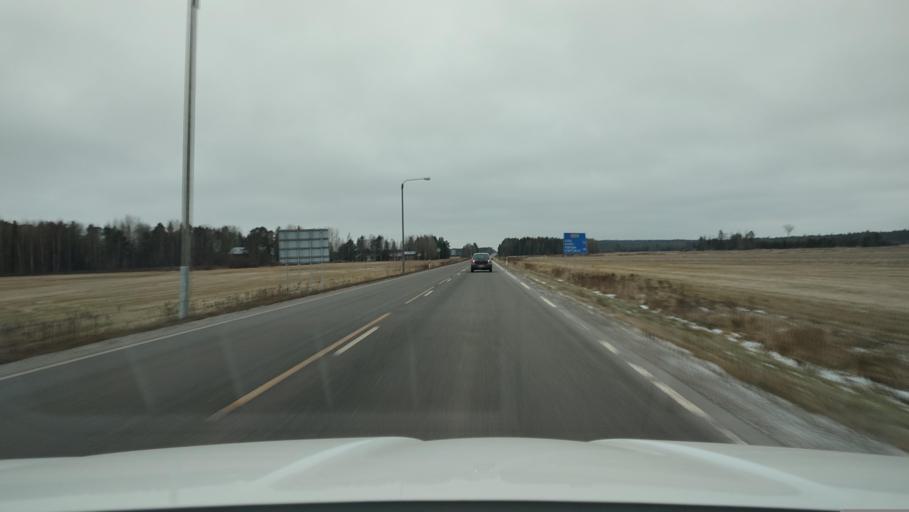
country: FI
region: Ostrobothnia
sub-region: Sydosterbotten
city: Naerpes
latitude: 62.4740
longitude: 21.4370
